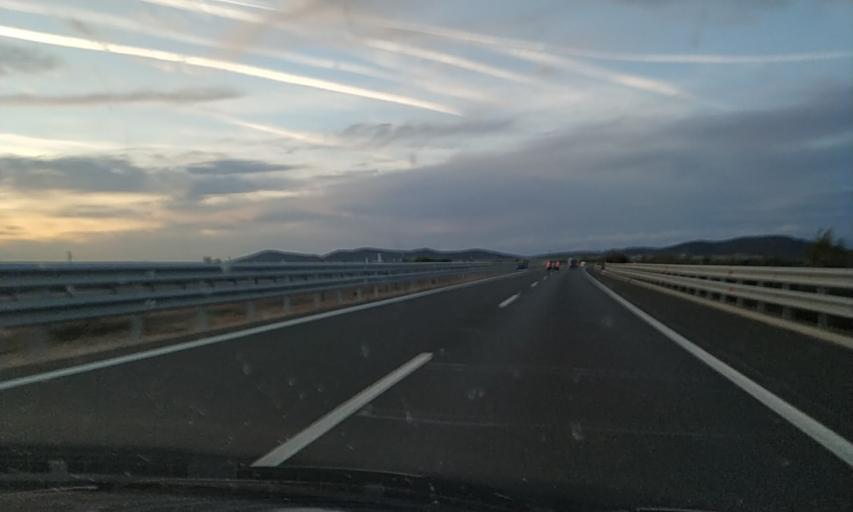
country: ES
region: Extremadura
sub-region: Provincia de Caceres
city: Aldea del Cano
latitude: 39.3687
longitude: -6.3411
